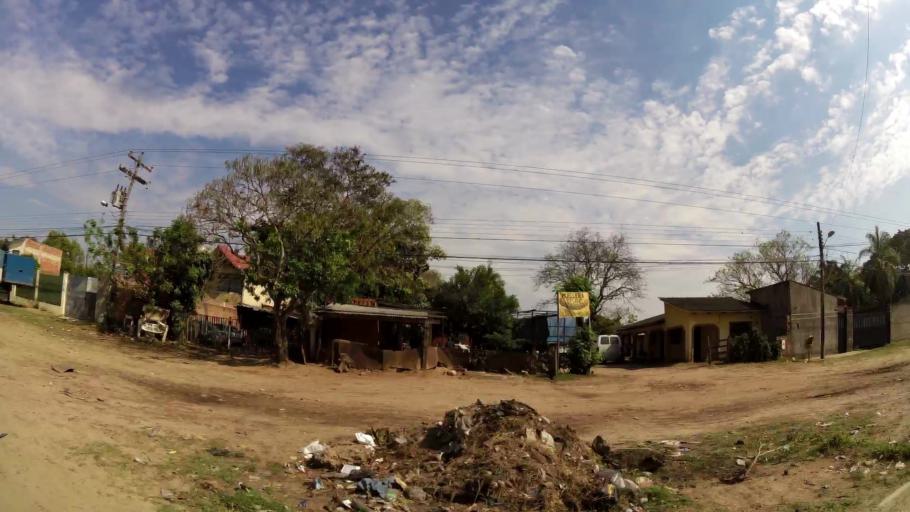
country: BO
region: Santa Cruz
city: Santa Cruz de la Sierra
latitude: -17.7255
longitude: -63.1574
